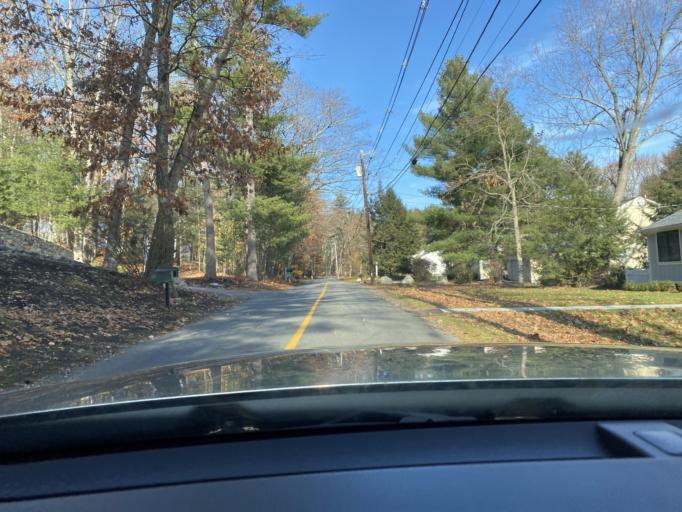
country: US
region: Massachusetts
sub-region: Norfolk County
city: Medfield
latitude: 42.1880
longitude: -71.2826
